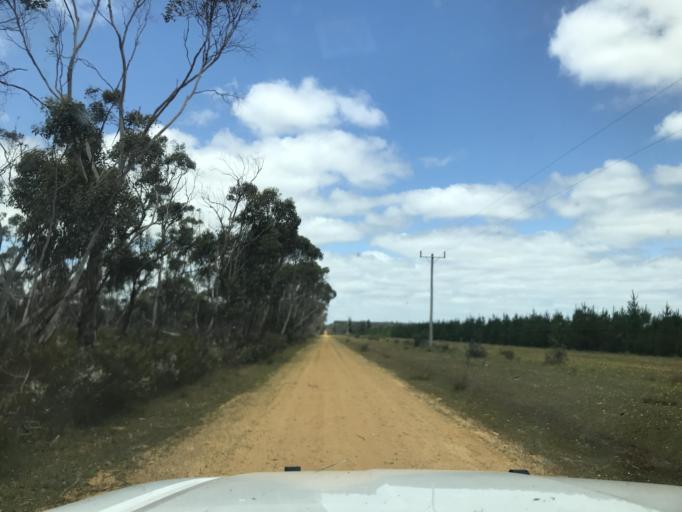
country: AU
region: South Australia
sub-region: Wattle Range
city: Penola
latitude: -37.3649
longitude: 141.1545
